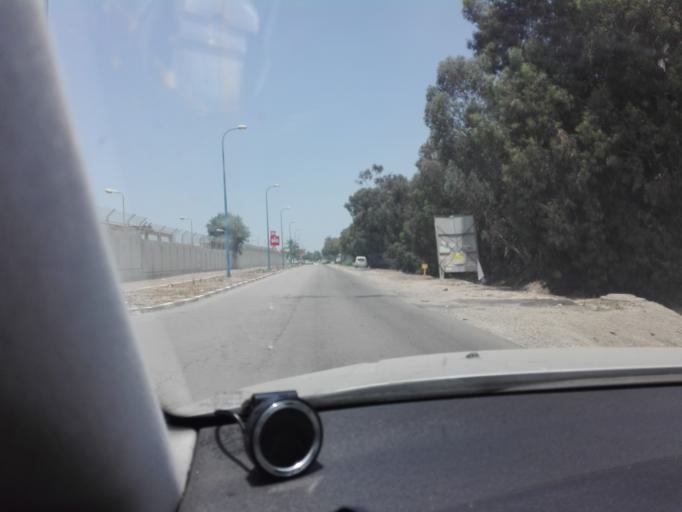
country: IL
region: Central District
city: Bene 'Ayish
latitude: 31.7250
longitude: 34.7550
